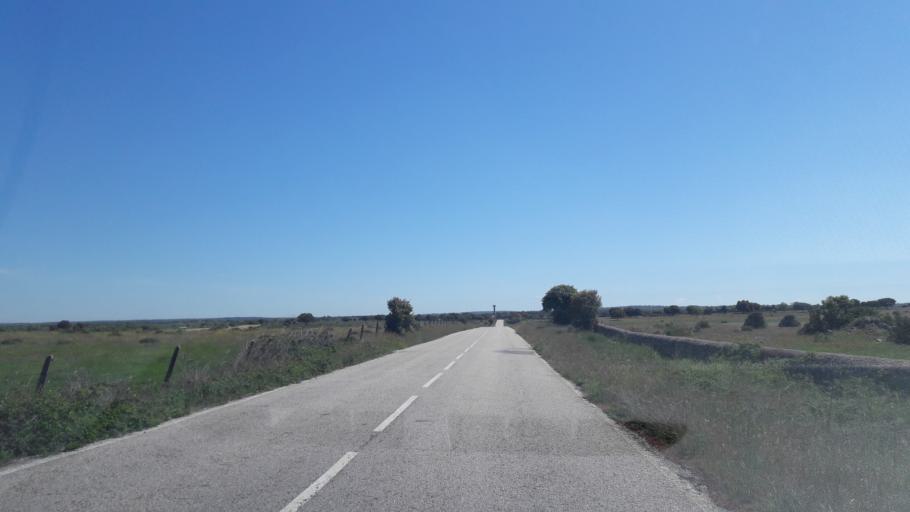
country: ES
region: Castille and Leon
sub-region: Provincia de Salamanca
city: Villarmuerto
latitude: 41.0504
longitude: -6.3773
